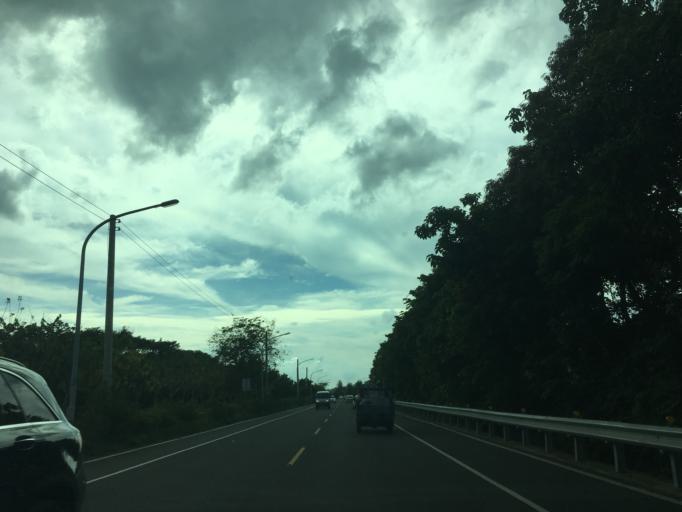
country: TW
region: Taiwan
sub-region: Chiayi
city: Jiayi Shi
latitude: 23.4446
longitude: 120.5886
